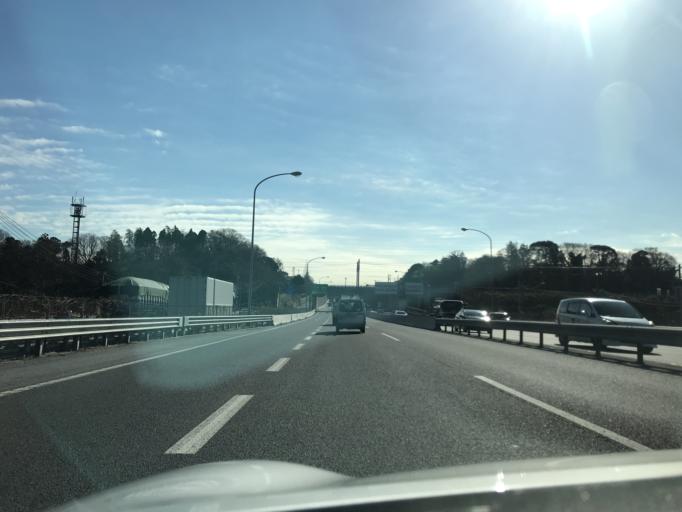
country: JP
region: Chiba
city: Chiba
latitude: 35.6276
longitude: 140.1347
